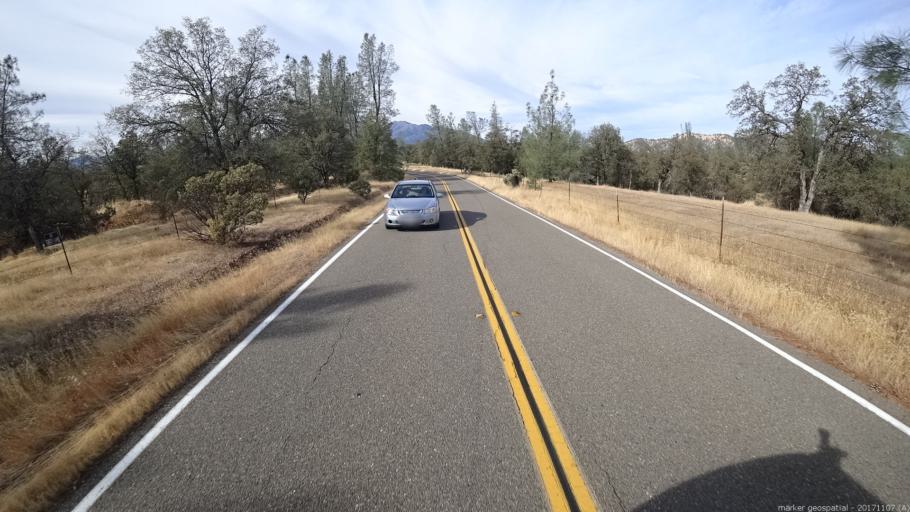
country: US
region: California
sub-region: Shasta County
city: Shasta
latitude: 40.4942
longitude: -122.5177
